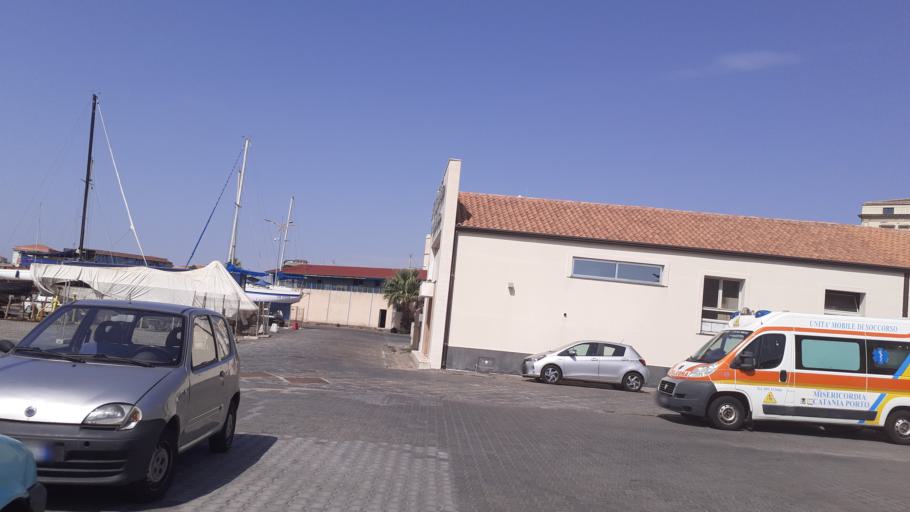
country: IT
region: Sicily
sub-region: Catania
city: Catania
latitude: 37.5020
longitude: 15.0969
